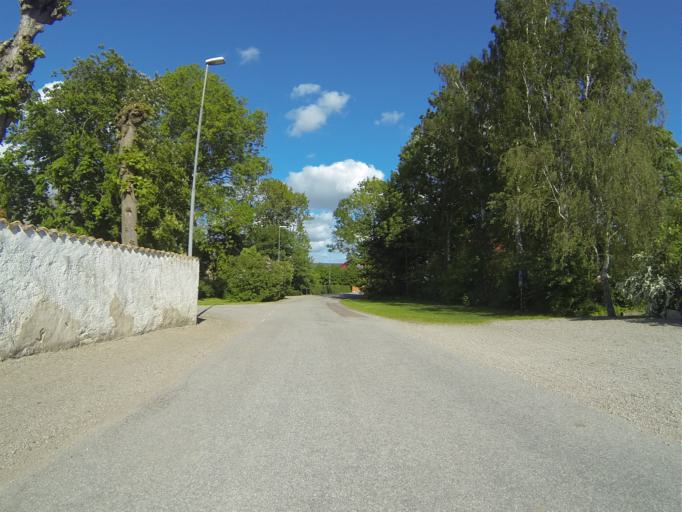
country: SE
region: Skane
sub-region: Lunds Kommun
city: Lund
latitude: 55.6755
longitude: 13.1998
